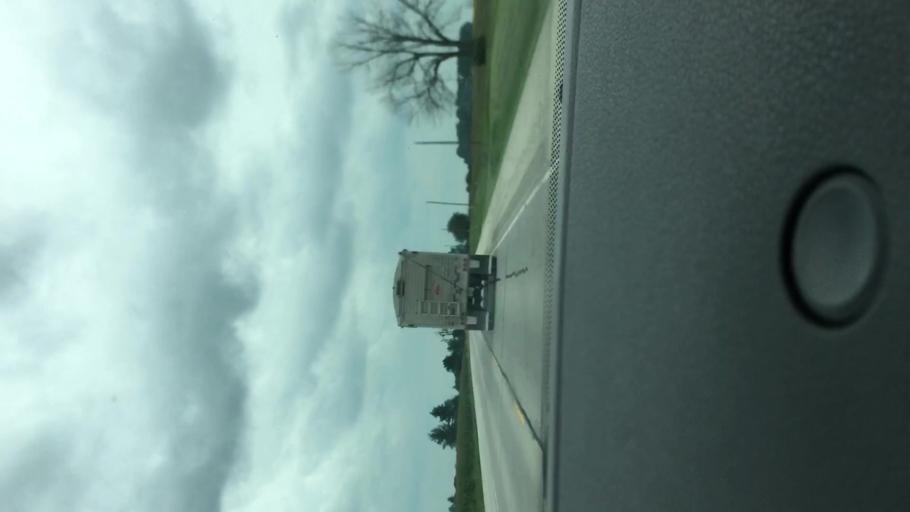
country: US
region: Indiana
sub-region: Jay County
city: Portland
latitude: 40.3371
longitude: -84.9773
